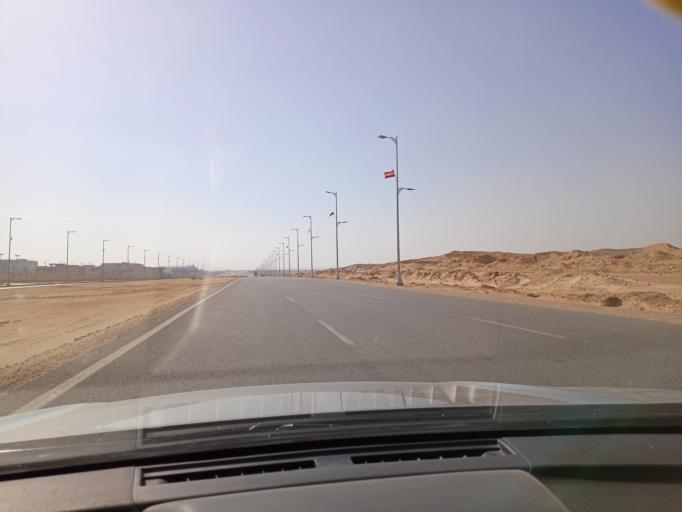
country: EG
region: Muhafazat al Qalyubiyah
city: Al Khankah
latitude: 30.0444
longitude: 31.7058
